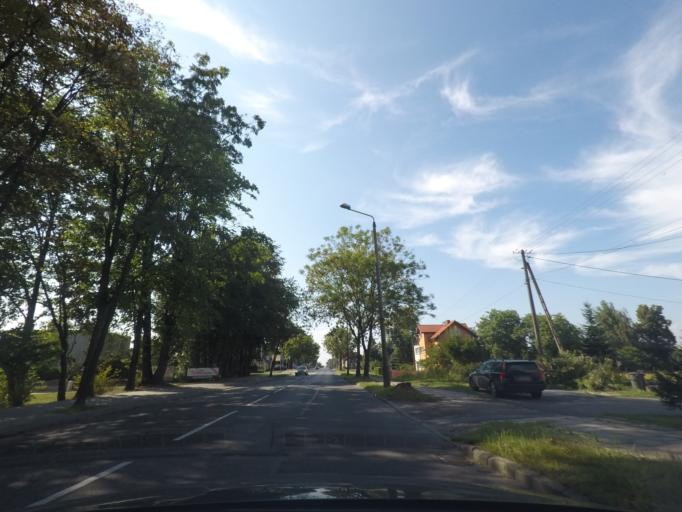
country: PL
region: Silesian Voivodeship
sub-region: Zory
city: Zory
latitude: 50.0504
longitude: 18.6881
